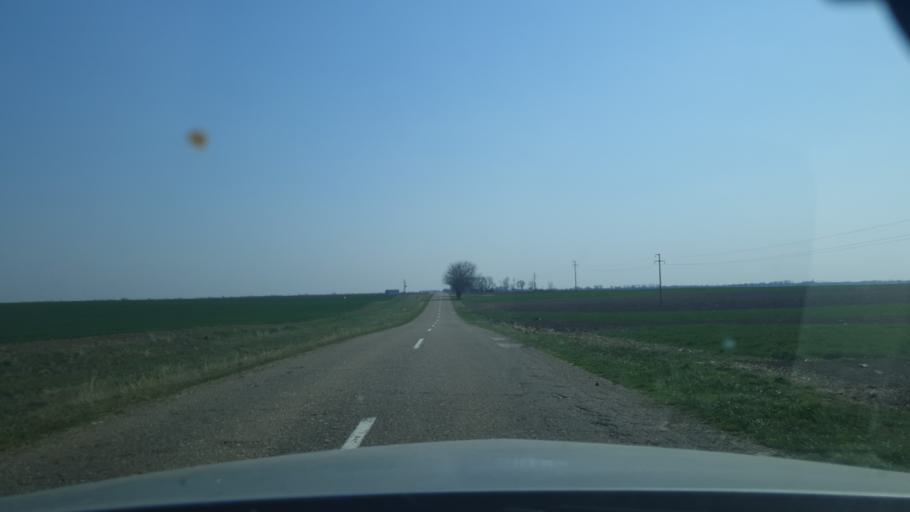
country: RS
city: Sasinci
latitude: 45.0352
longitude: 19.7425
